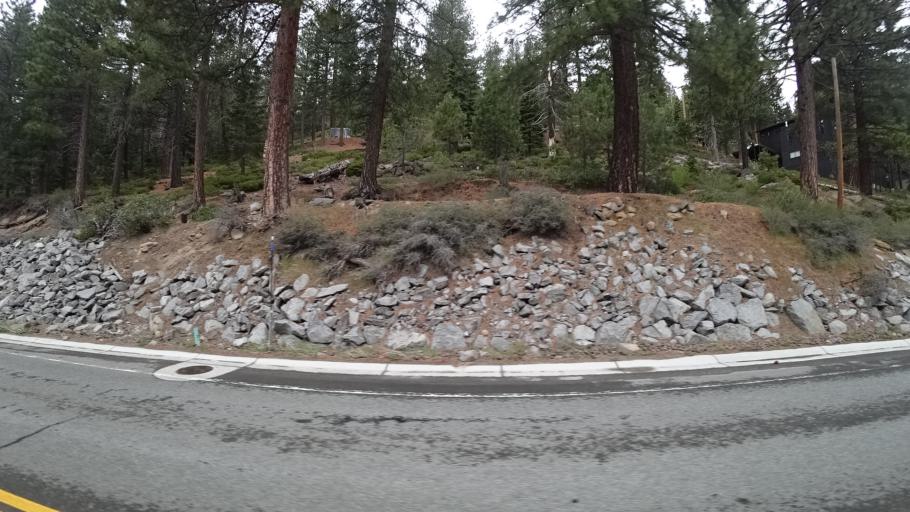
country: US
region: California
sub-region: Placer County
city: Kings Beach
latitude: 39.2330
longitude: -120.0030
